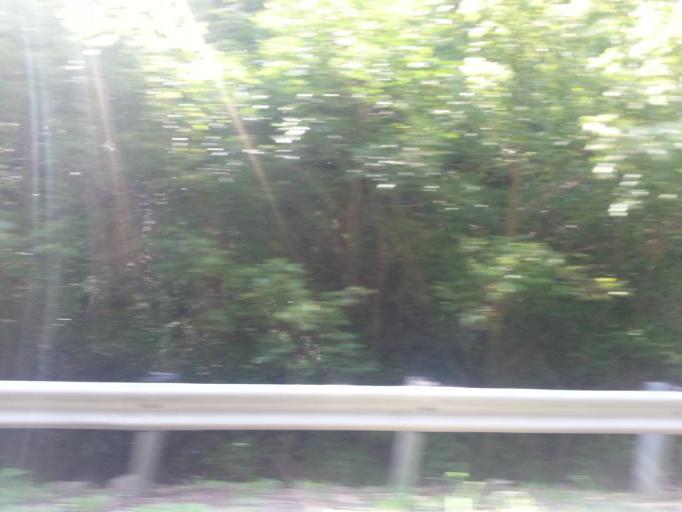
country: US
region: Virginia
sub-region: Washington County
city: Abingdon
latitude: 36.6797
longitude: -81.9733
